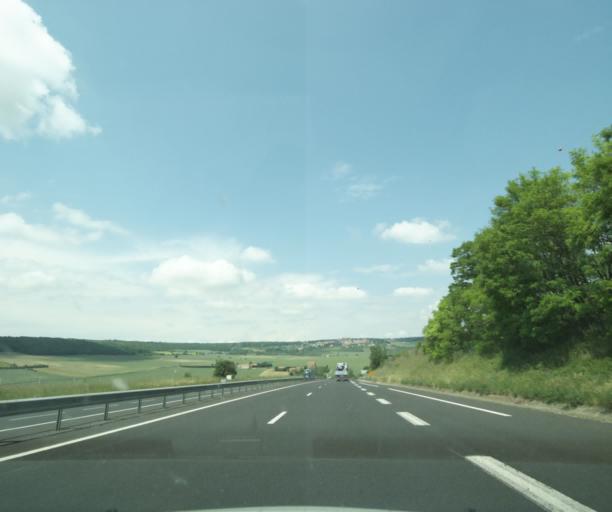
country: FR
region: Auvergne
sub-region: Departement du Puy-de-Dome
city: Le Breuil-sur-Couze
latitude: 45.4763
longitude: 3.2463
